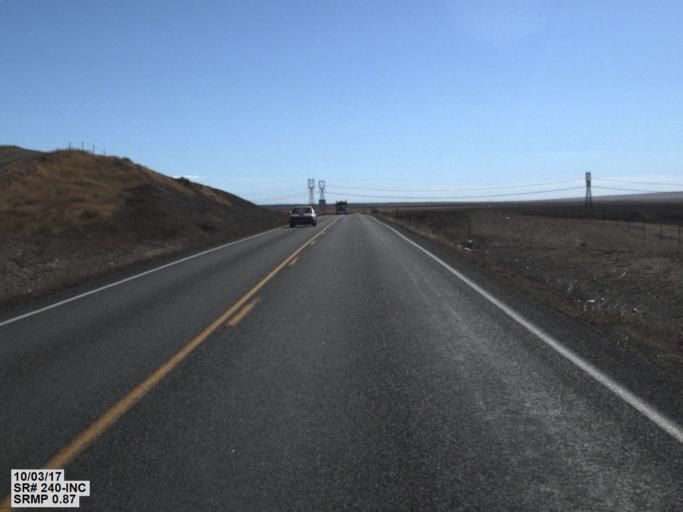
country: US
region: Washington
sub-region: Grant County
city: Desert Aire
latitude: 46.5663
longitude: -119.7213
